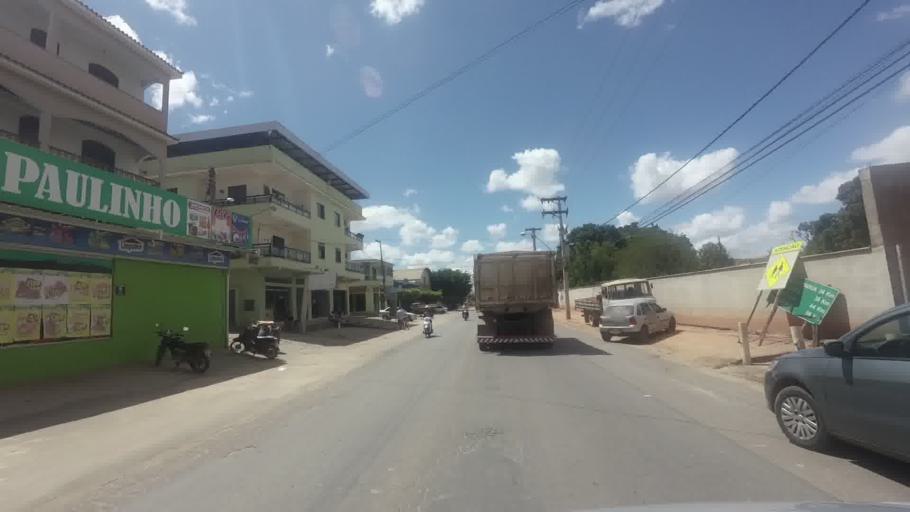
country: BR
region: Minas Gerais
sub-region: Recreio
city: Recreio
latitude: -21.6584
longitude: -42.3395
